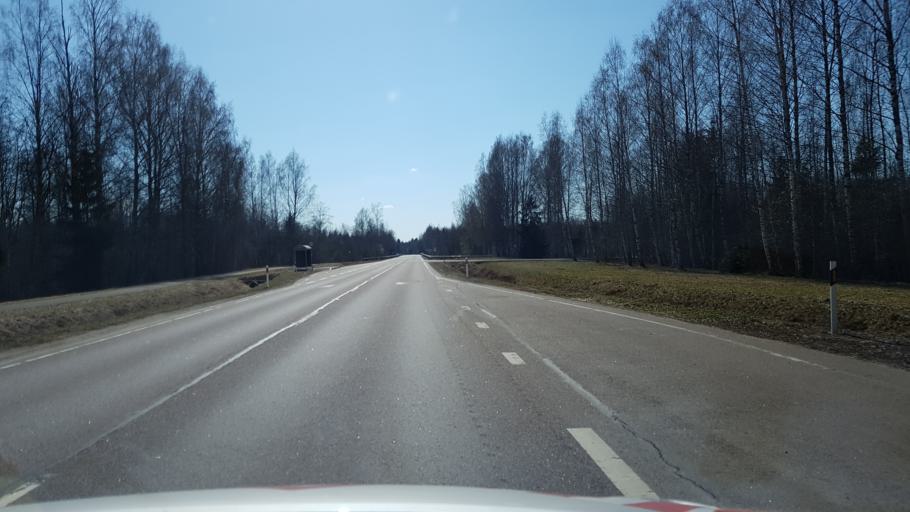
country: EE
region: Jogevamaa
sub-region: Mustvee linn
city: Mustvee
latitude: 58.7707
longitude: 26.9044
